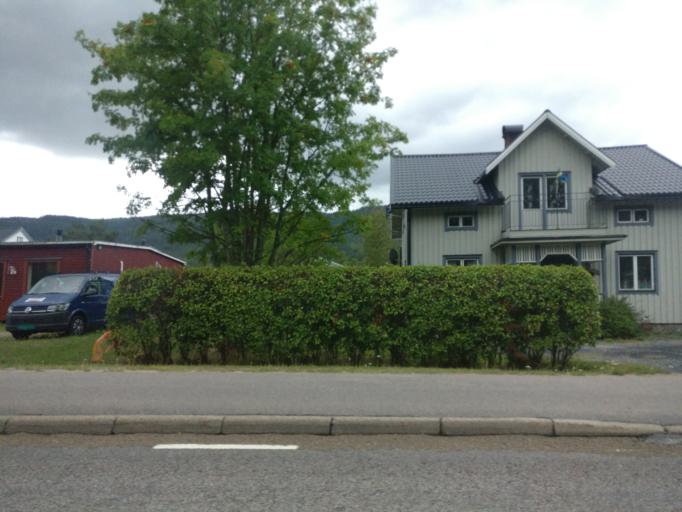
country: SE
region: Vaermland
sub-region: Torsby Kommun
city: Torsby
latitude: 60.7283
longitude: 12.8730
